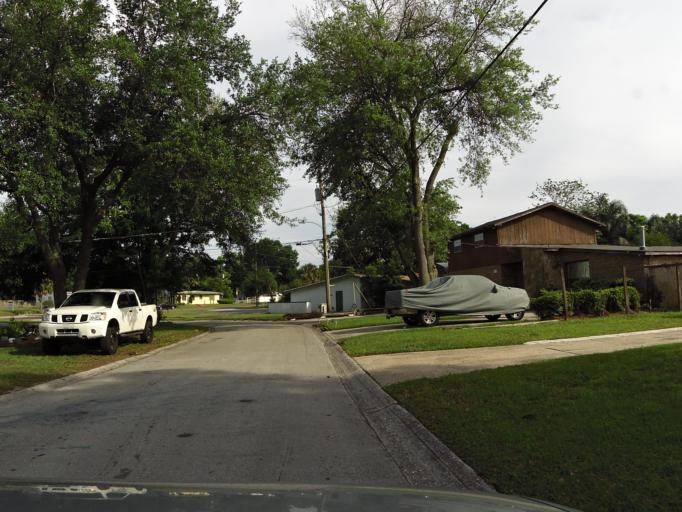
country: US
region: Florida
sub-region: Duval County
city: Jacksonville
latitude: 30.3400
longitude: -81.5899
